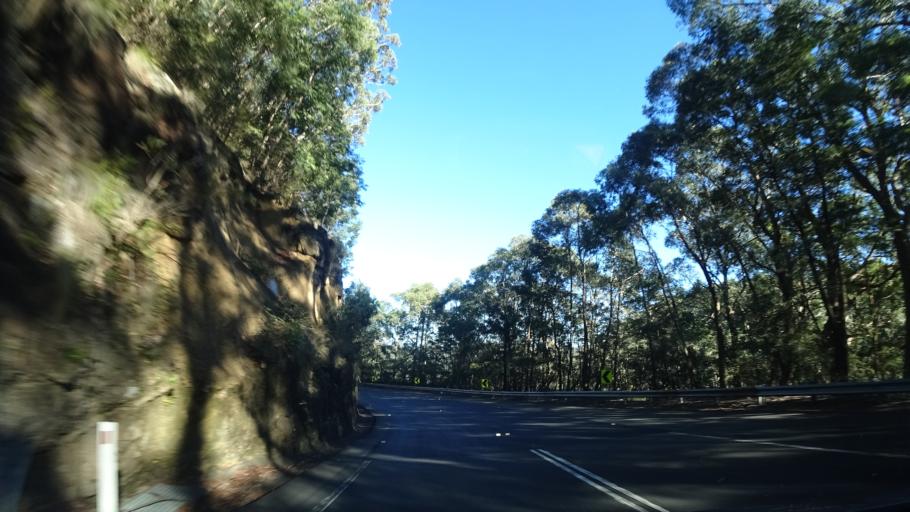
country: AU
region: New South Wales
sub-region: Blue Mountains Municipality
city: Blackheath
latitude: -33.5477
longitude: 150.4161
